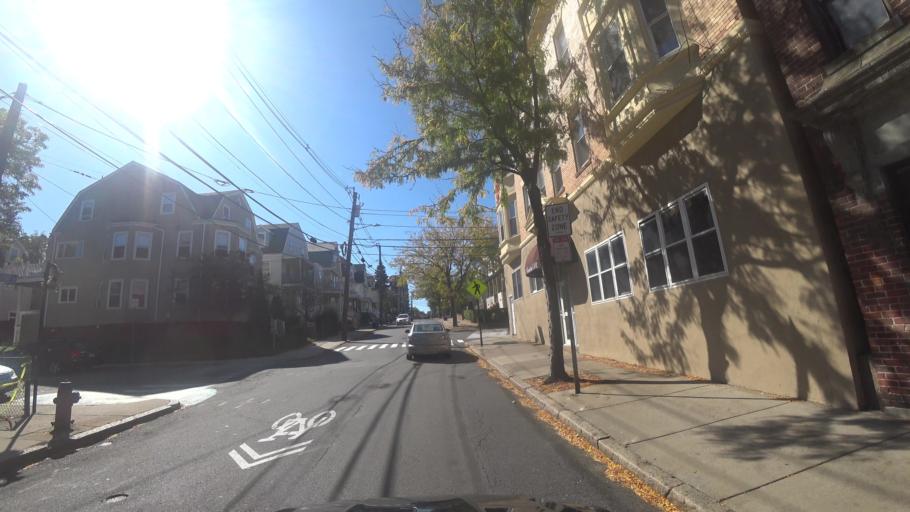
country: US
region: Massachusetts
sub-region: Middlesex County
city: Somerville
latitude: 42.3902
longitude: -71.1023
